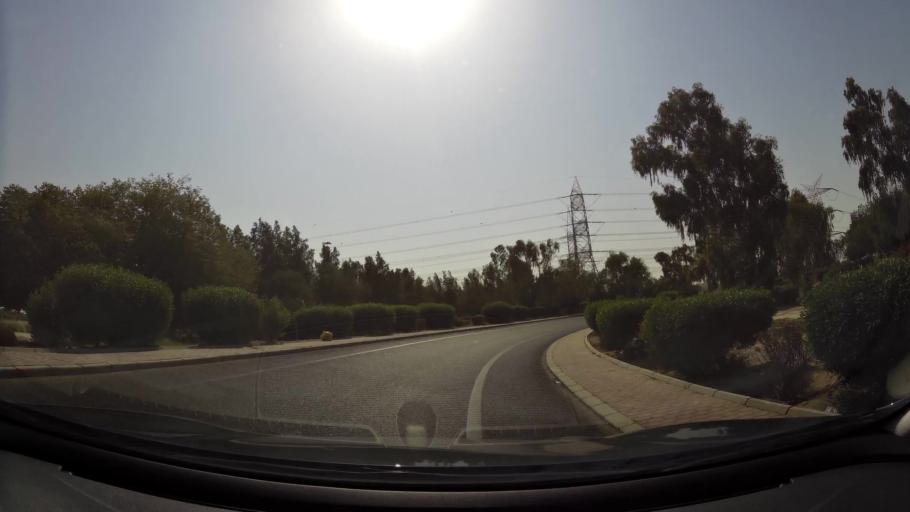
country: KW
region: Mubarak al Kabir
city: Sabah as Salim
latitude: 29.2634
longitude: 48.0422
